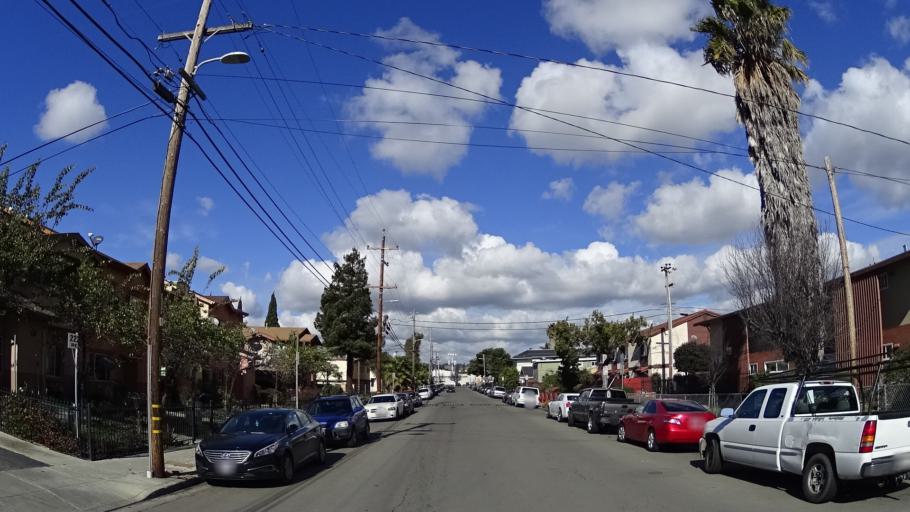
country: US
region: California
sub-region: Alameda County
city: Cherryland
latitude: 37.6641
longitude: -122.1086
